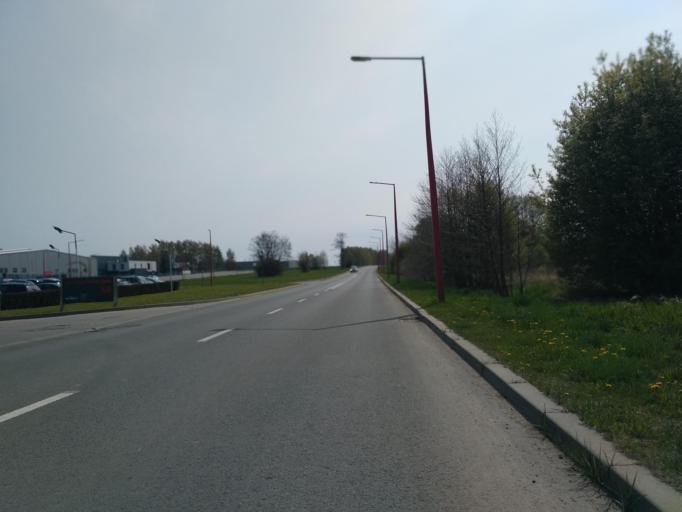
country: PL
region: Subcarpathian Voivodeship
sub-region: Krosno
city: Krosno
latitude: 49.6767
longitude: 21.7310
